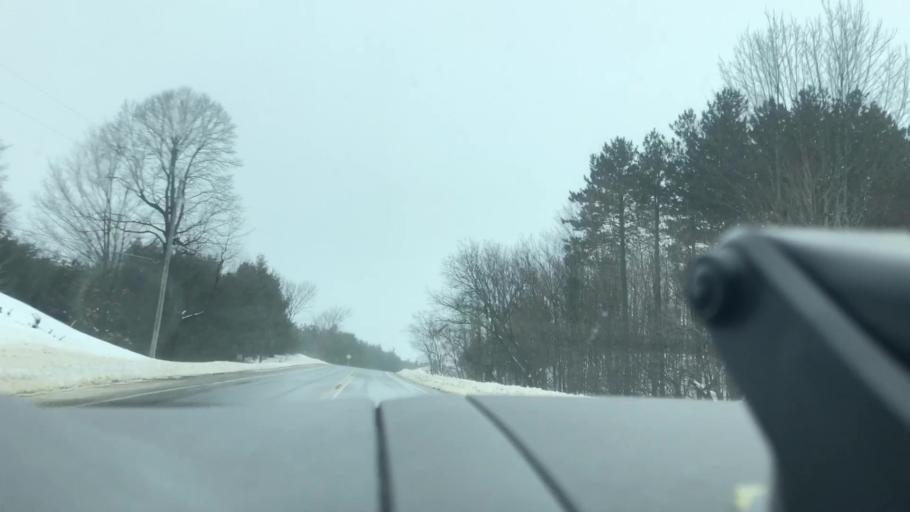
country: US
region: Michigan
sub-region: Charlevoix County
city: East Jordan
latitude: 45.1573
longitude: -85.1589
